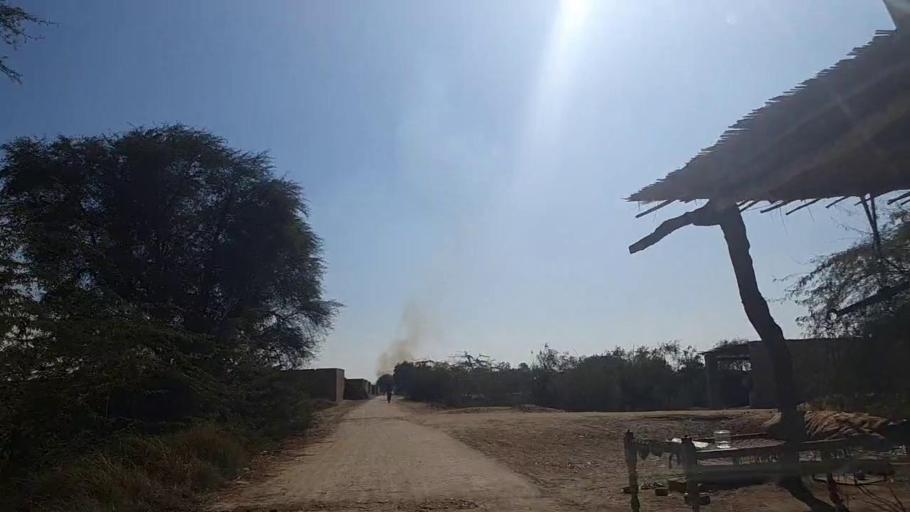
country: PK
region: Sindh
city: Sakrand
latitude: 26.2536
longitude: 68.1925
